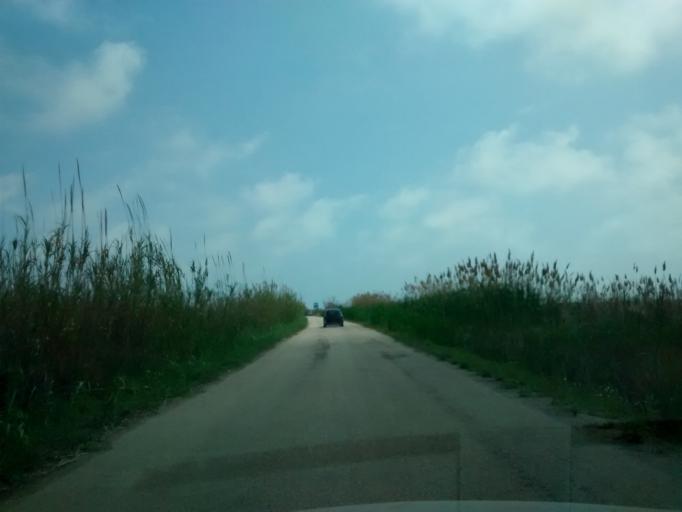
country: ES
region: Catalonia
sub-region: Provincia de Tarragona
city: Deltebre
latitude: 40.6914
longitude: 0.8431
